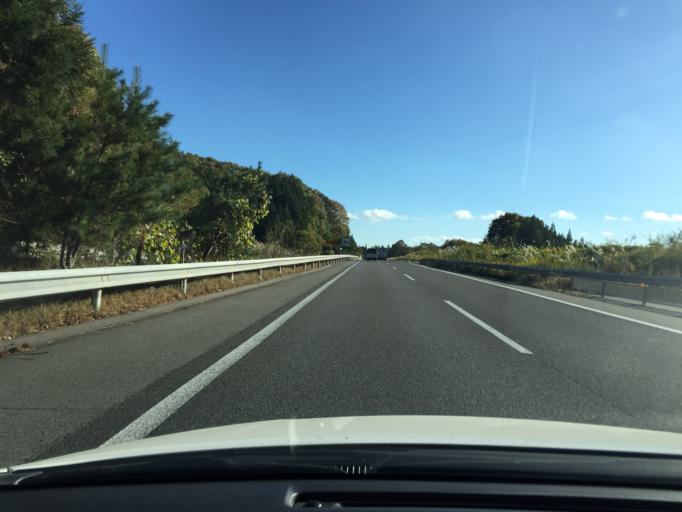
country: JP
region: Fukushima
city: Funehikimachi-funehiki
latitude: 37.3466
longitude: 140.6085
